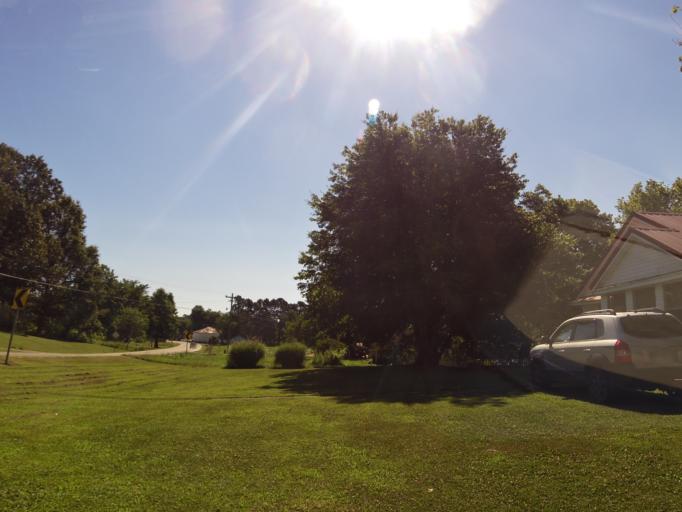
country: US
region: Arkansas
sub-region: Clay County
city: Piggott
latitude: 36.4291
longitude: -90.2714
